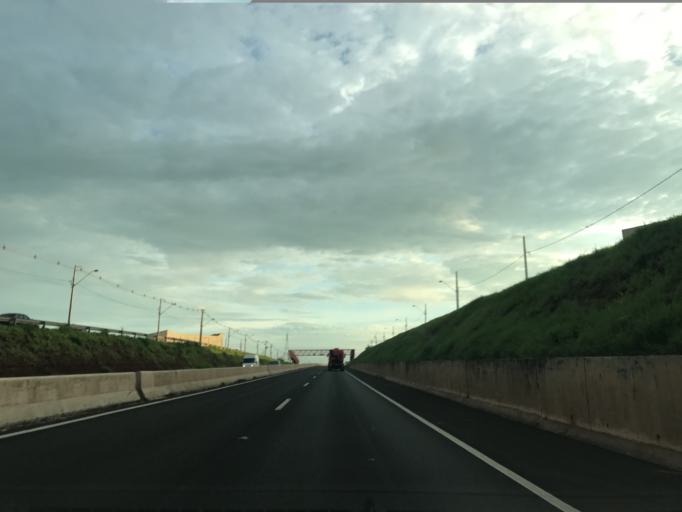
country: BR
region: Parana
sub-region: Maringa
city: Maringa
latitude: -23.3846
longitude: -51.9641
